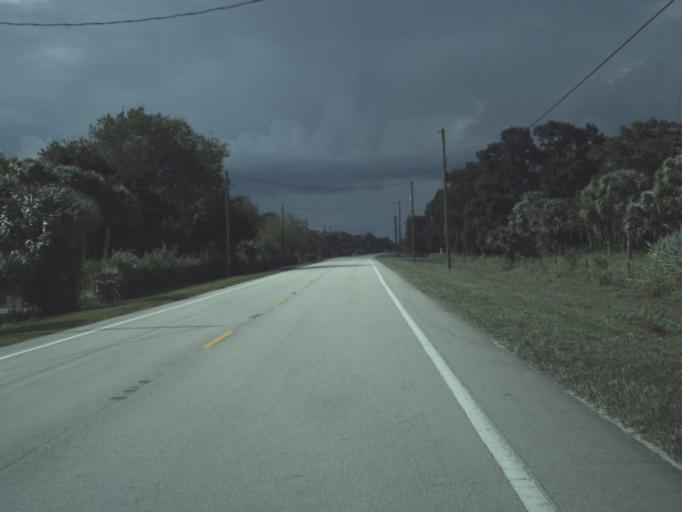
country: US
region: Florida
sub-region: Okeechobee County
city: Taylor Creek
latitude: 27.1647
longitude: -80.7163
